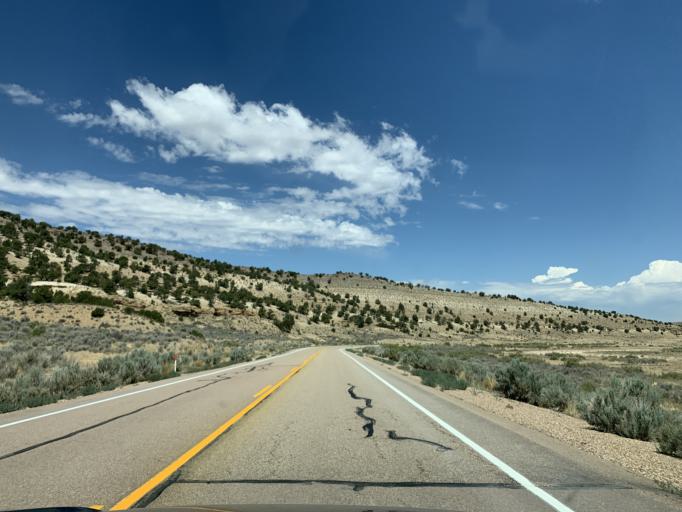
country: US
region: Utah
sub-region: Duchesne County
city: Duchesne
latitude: 39.9839
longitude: -110.1621
